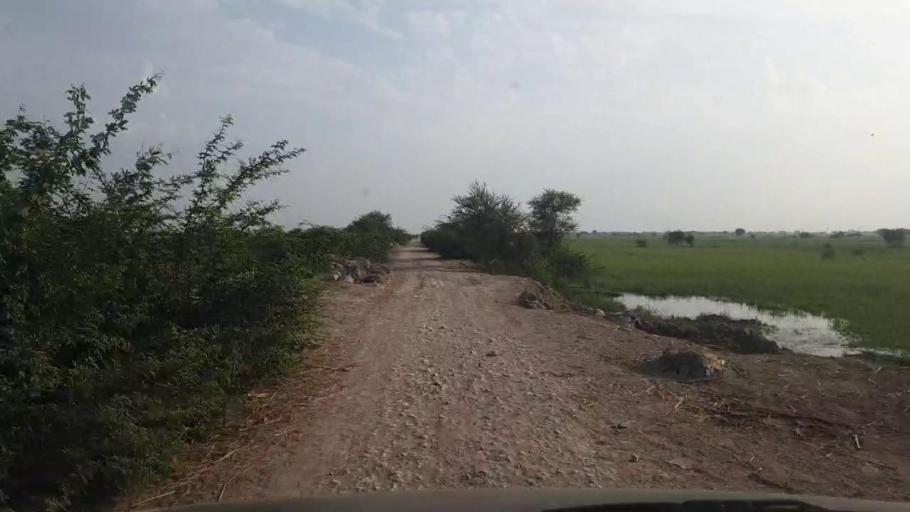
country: PK
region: Sindh
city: Badin
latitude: 24.5651
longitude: 68.6675
